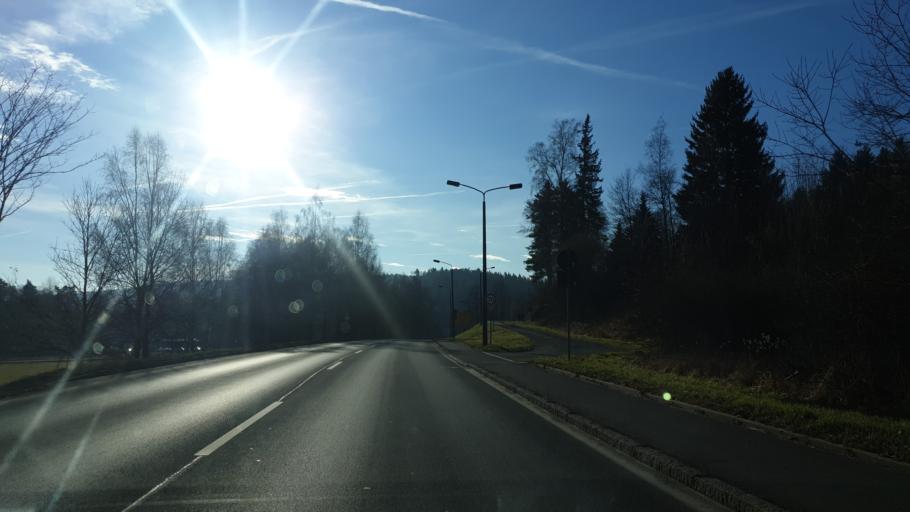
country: DE
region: Saxony
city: Adorf
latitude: 50.3032
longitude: 12.2529
